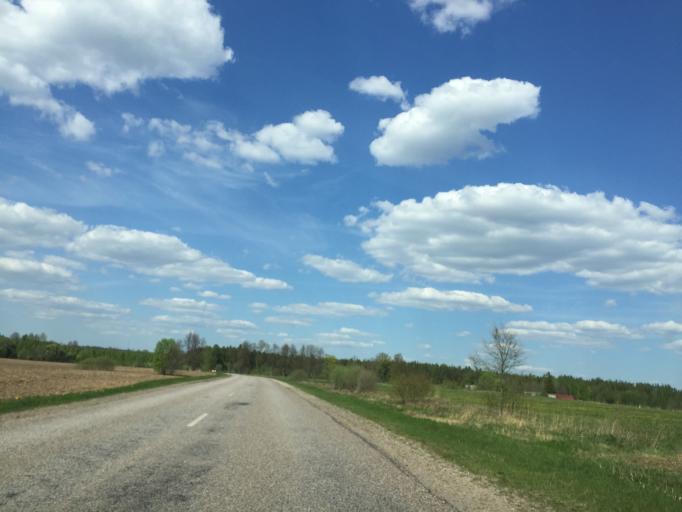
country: LV
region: Limbazu Rajons
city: Limbazi
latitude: 57.3862
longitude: 24.6881
